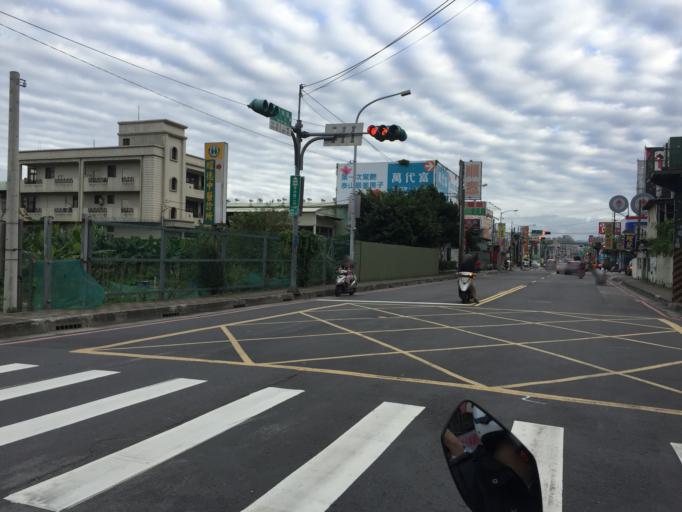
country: TW
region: Taipei
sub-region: Taipei
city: Banqiao
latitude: 25.0582
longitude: 121.4352
